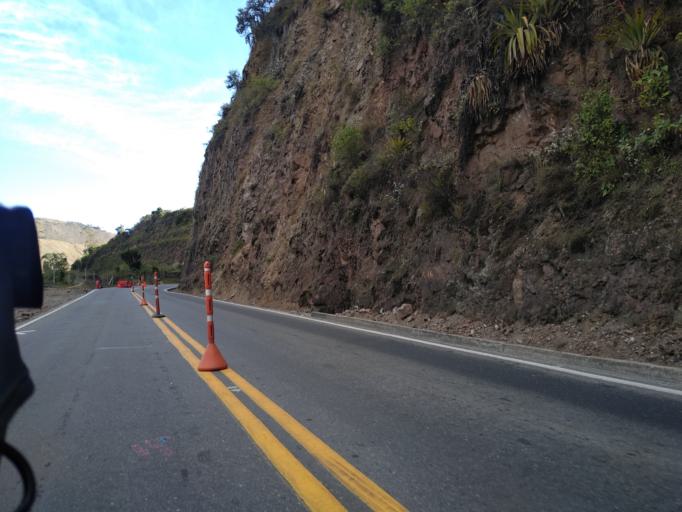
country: CO
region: Narino
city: Imues
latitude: 1.0556
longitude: -77.4496
